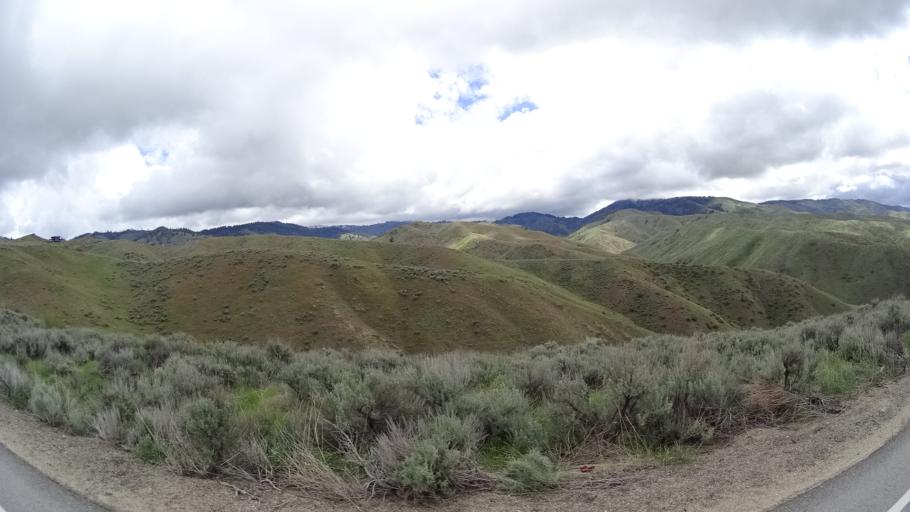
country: US
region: Idaho
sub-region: Ada County
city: Boise
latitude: 43.7051
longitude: -116.1655
